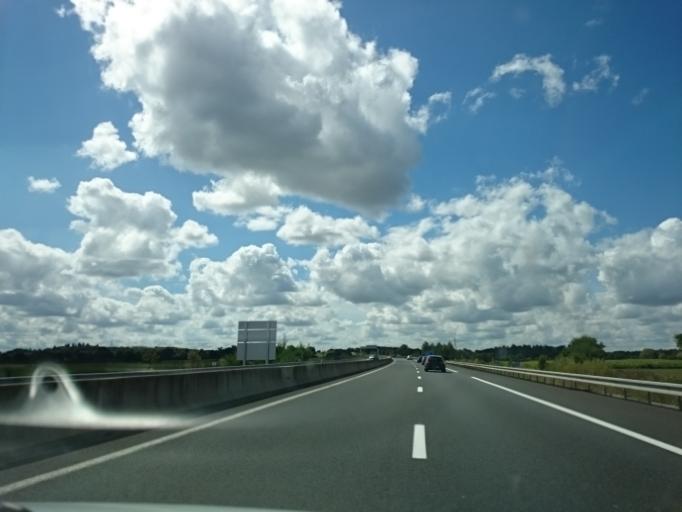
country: FR
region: Pays de la Loire
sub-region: Departement de Maine-et-Loire
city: Beaucouze
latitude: 47.4921
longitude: -0.6415
